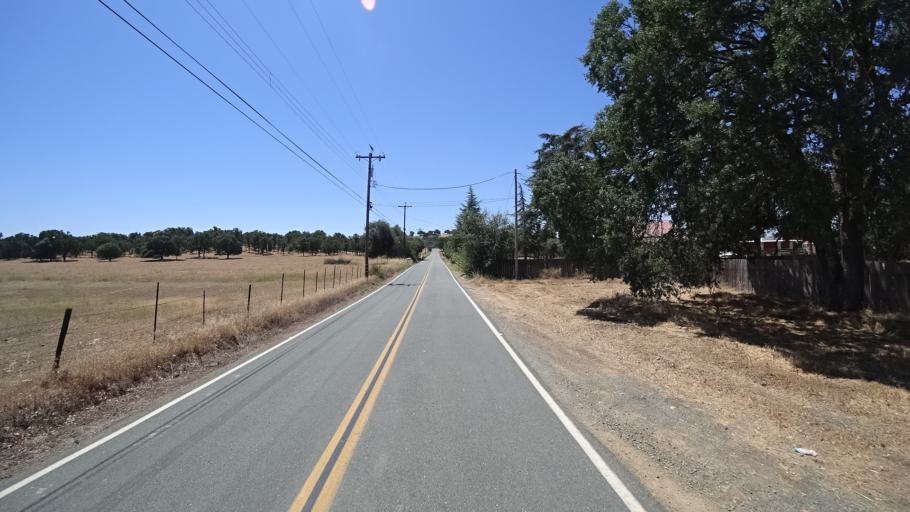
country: US
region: California
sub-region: Calaveras County
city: Rancho Calaveras
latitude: 38.1372
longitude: -120.9133
